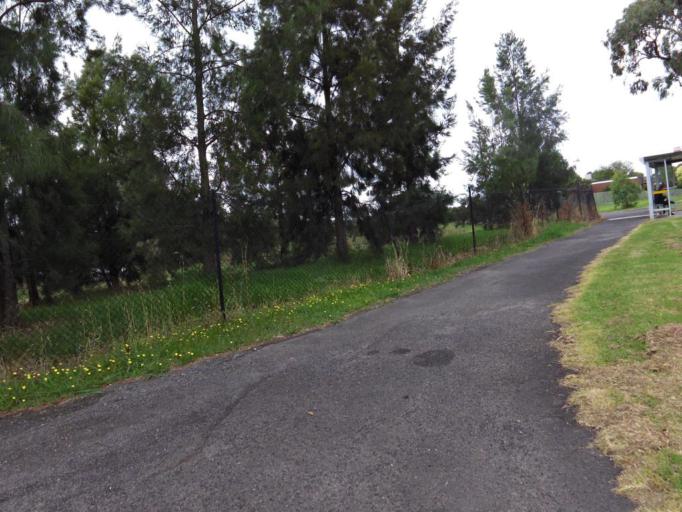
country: AU
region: Victoria
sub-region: Knox
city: Knoxfield
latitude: -37.9090
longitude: 145.2532
